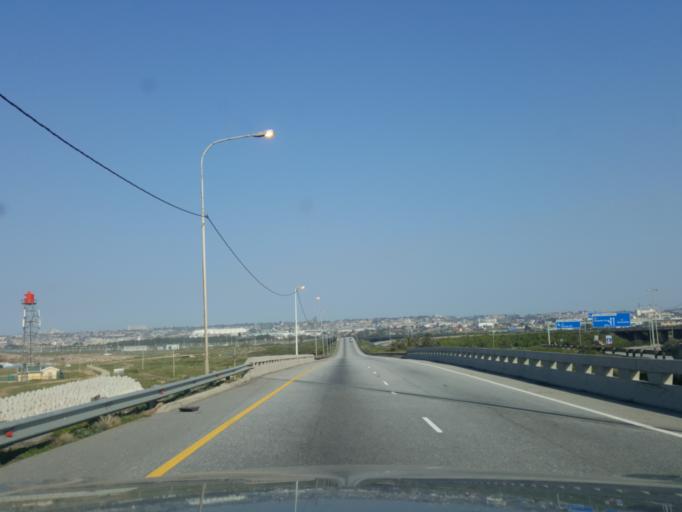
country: ZA
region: Eastern Cape
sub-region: Nelson Mandela Bay Metropolitan Municipality
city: Port Elizabeth
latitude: -33.9137
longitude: 25.6149
